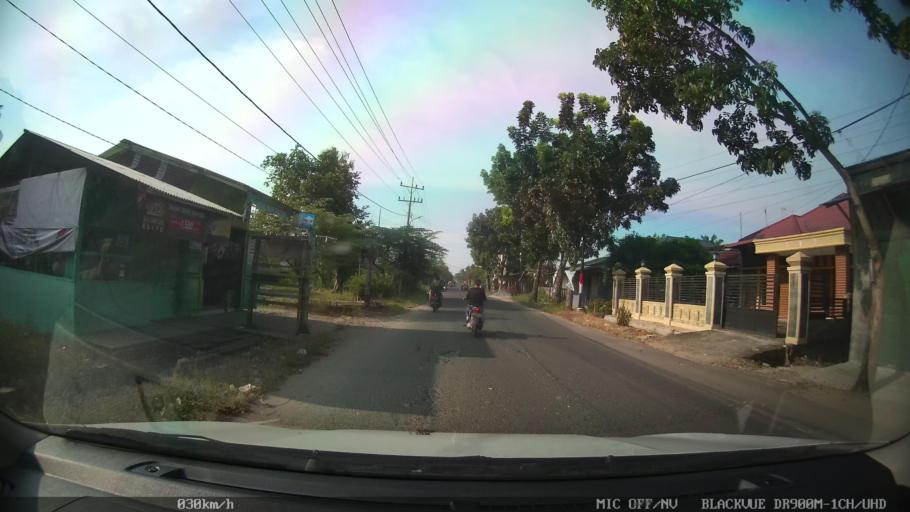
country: ID
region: North Sumatra
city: Binjai
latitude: 3.6198
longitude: 98.5184
